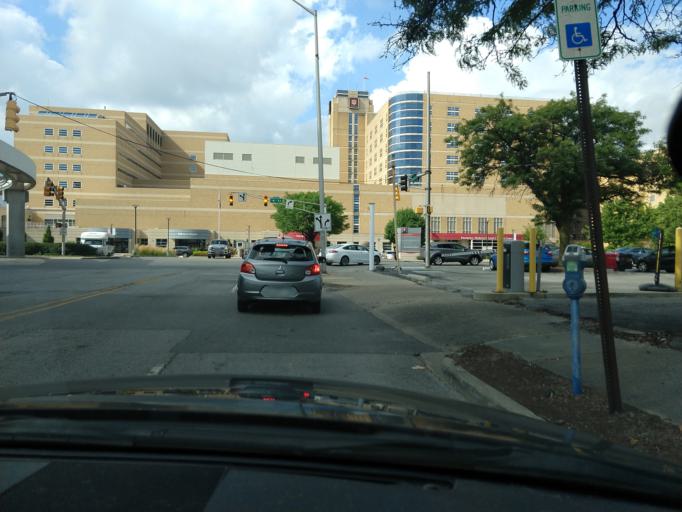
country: US
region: Indiana
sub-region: Marion County
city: Indianapolis
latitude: 39.7880
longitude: -86.1630
